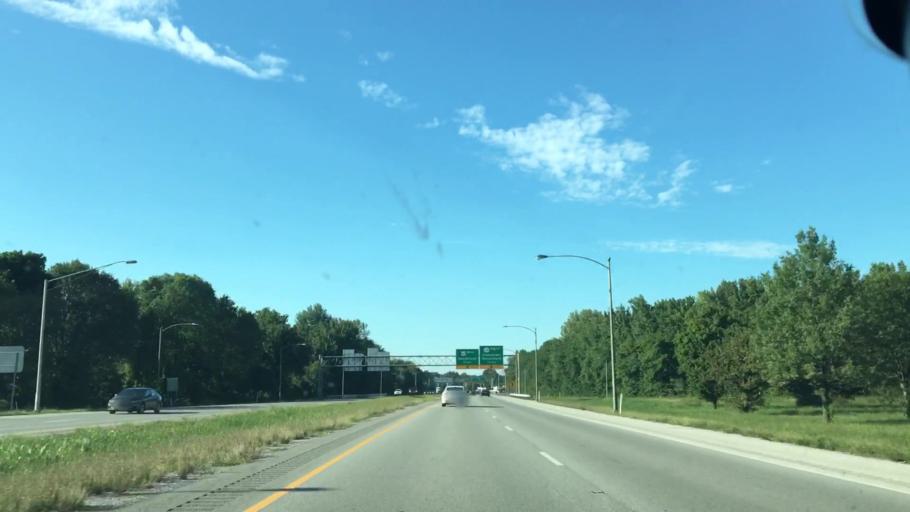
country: US
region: Kentucky
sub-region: Daviess County
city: Owensboro
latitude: 37.7680
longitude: -87.1642
